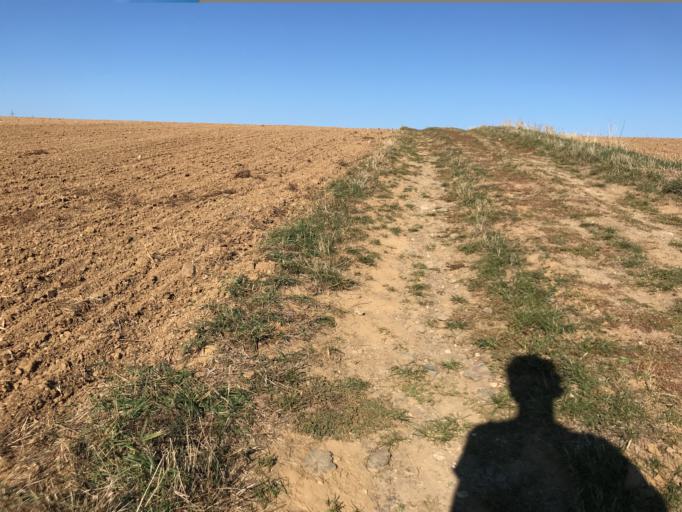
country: DE
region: Rheinland-Pfalz
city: Kobern-Gondorf
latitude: 50.3156
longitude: 7.4376
